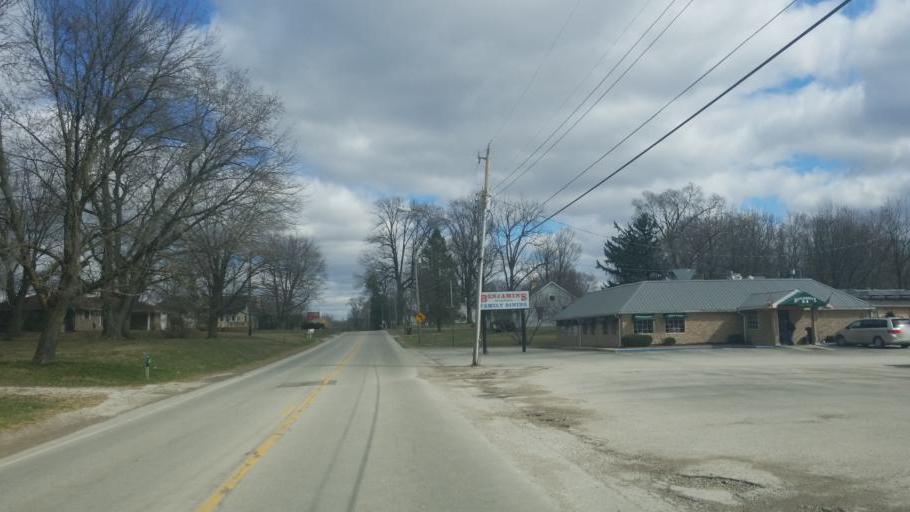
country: US
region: Indiana
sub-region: Parke County
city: Rockville
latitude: 39.7625
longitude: -87.2218
